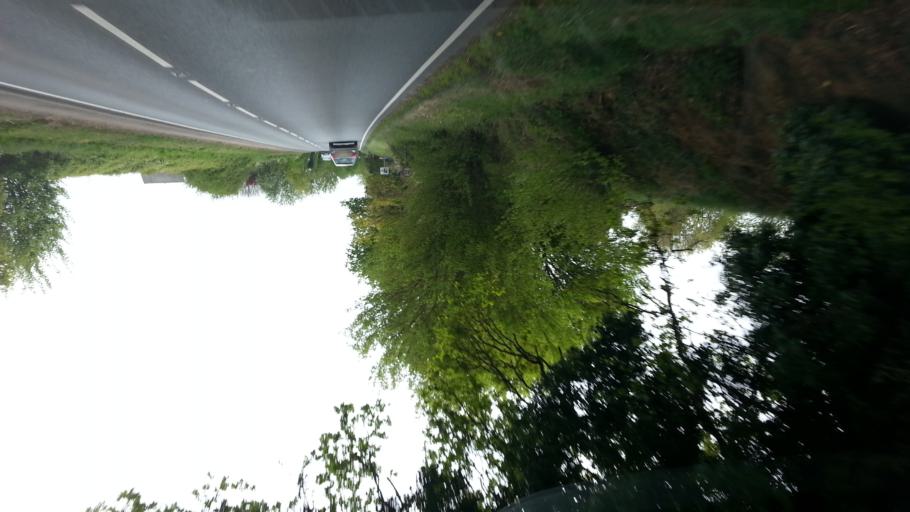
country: GB
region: England
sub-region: Suffolk
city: Bury St Edmunds
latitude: 52.2149
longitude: 0.7453
